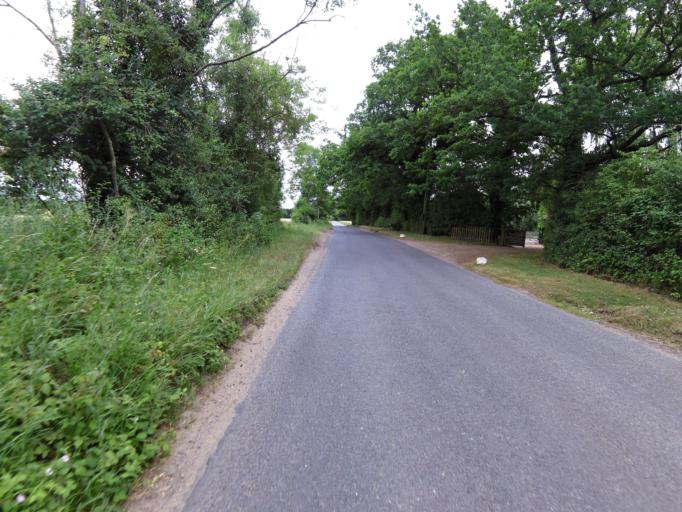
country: GB
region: England
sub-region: Norfolk
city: Harleston
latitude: 52.3976
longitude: 1.2408
